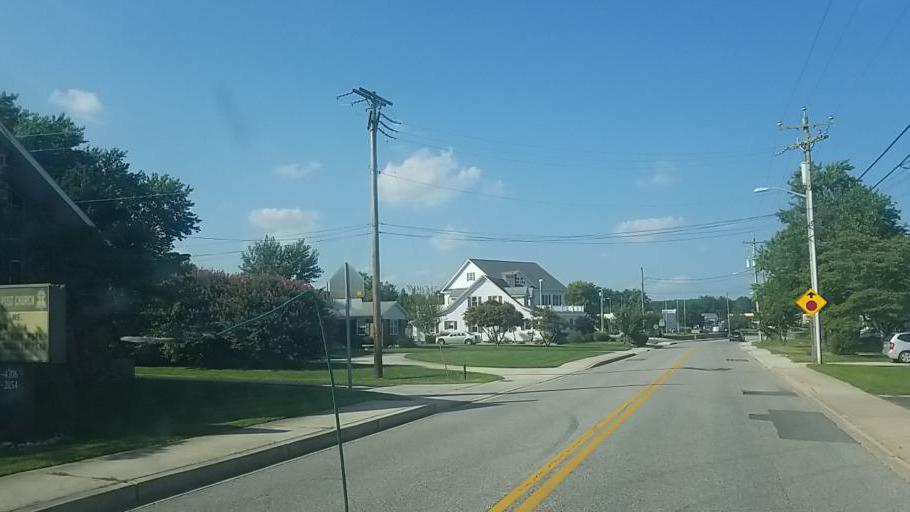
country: US
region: Maryland
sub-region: Worcester County
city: Berlin
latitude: 38.3329
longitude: -75.2135
